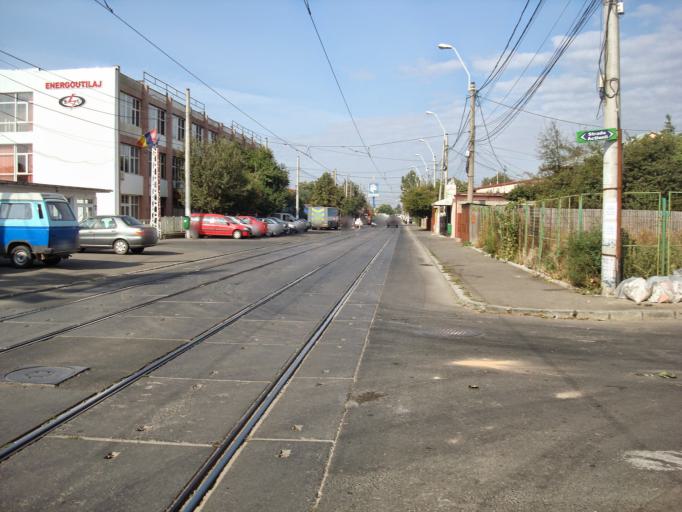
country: RO
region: Ilfov
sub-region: Comuna Jilava
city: Jilava
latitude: 44.3711
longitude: 26.0956
